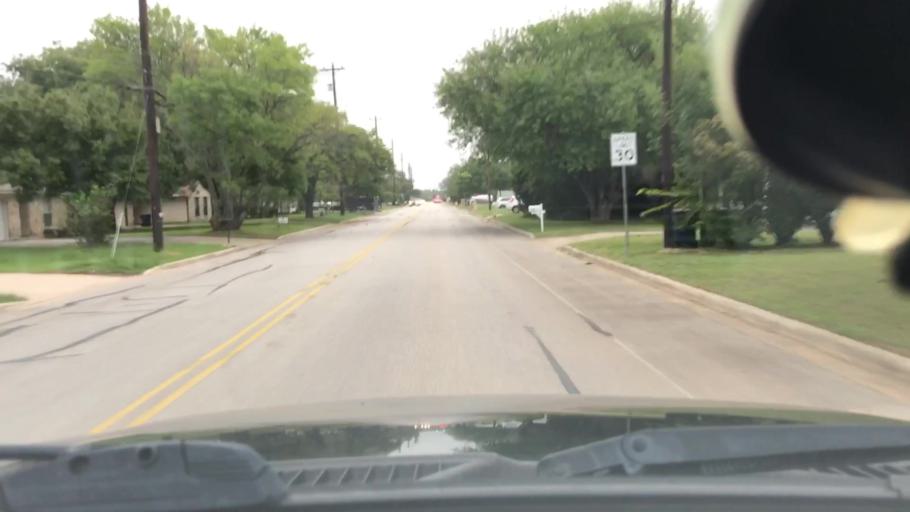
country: US
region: Texas
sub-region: Williamson County
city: Leander
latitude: 30.5433
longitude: -97.8444
